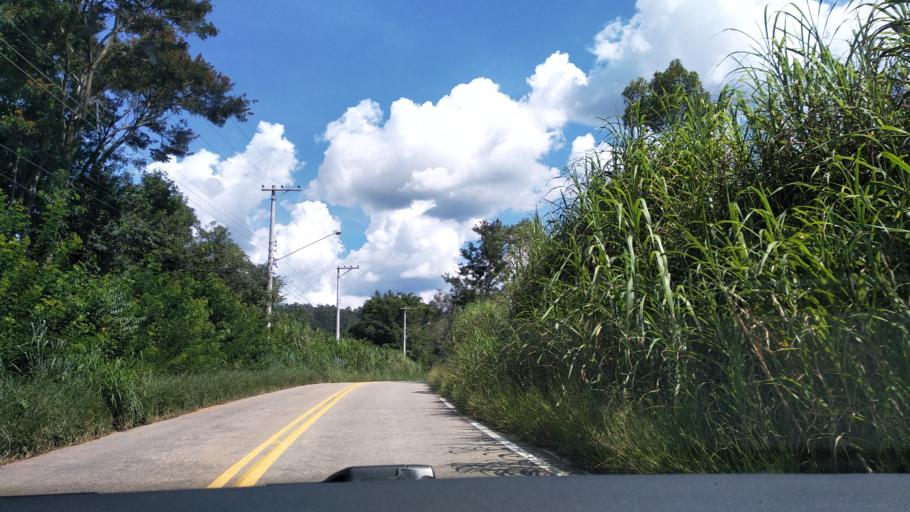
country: BR
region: Sao Paulo
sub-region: Varzea Paulista
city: Varzea Paulista
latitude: -23.2707
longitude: -46.8822
